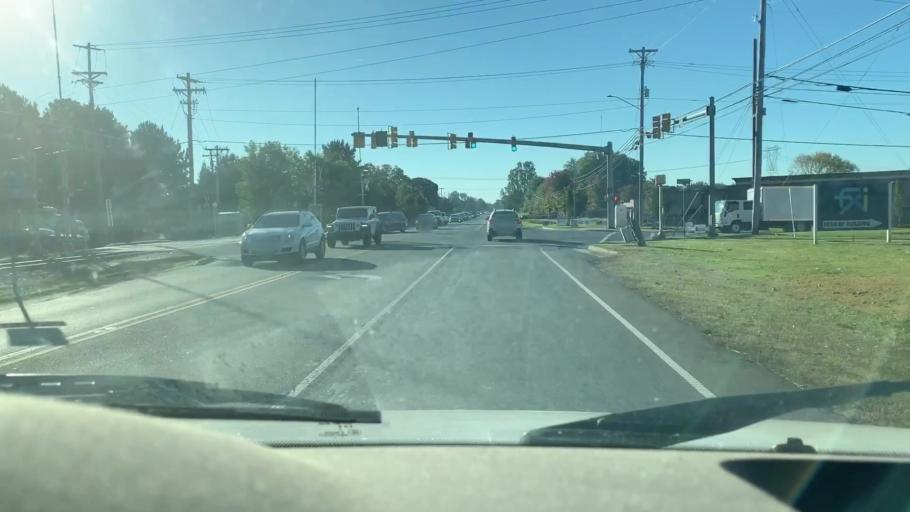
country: US
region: North Carolina
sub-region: Mecklenburg County
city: Cornelius
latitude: 35.4654
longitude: -80.8476
